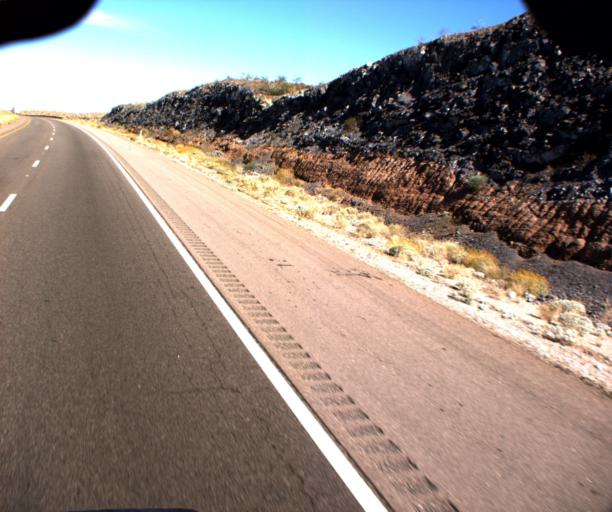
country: US
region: Nevada
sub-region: Clark County
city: Boulder City
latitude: 35.9517
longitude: -114.6494
